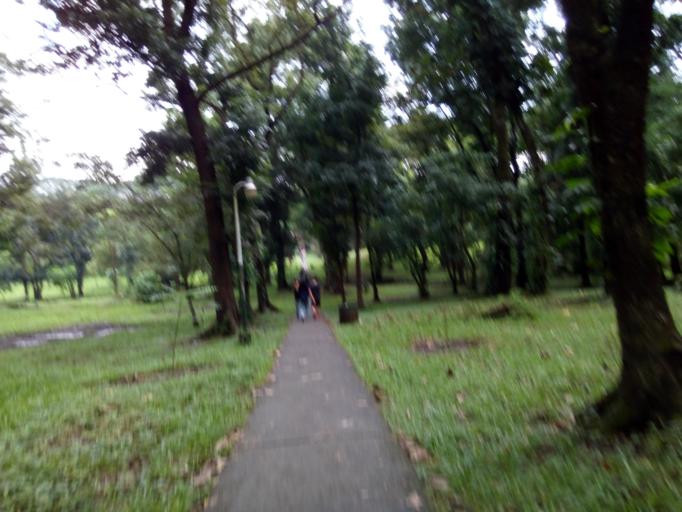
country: PH
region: Metro Manila
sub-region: Quezon City
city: Quezon City
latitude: 14.6543
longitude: 121.0698
